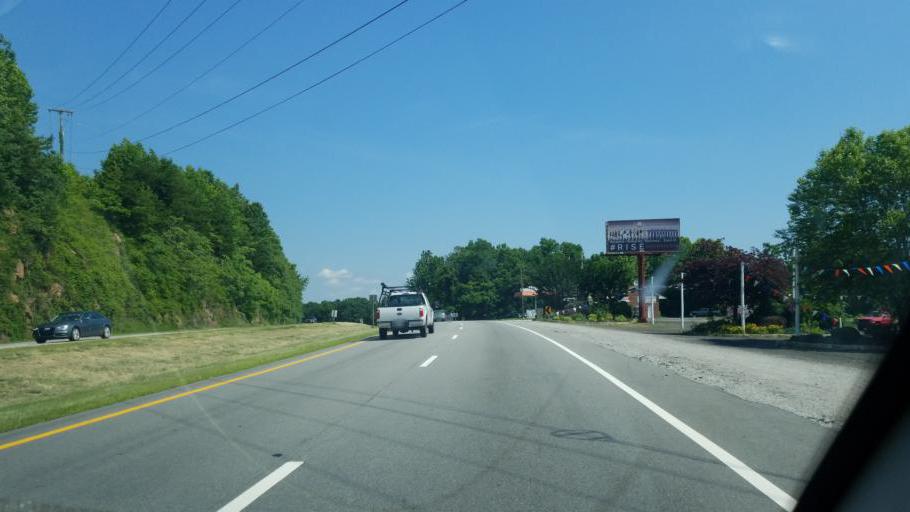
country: US
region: Virginia
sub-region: Pittsylvania County
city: Mount Hermon
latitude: 36.7436
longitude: -79.3780
